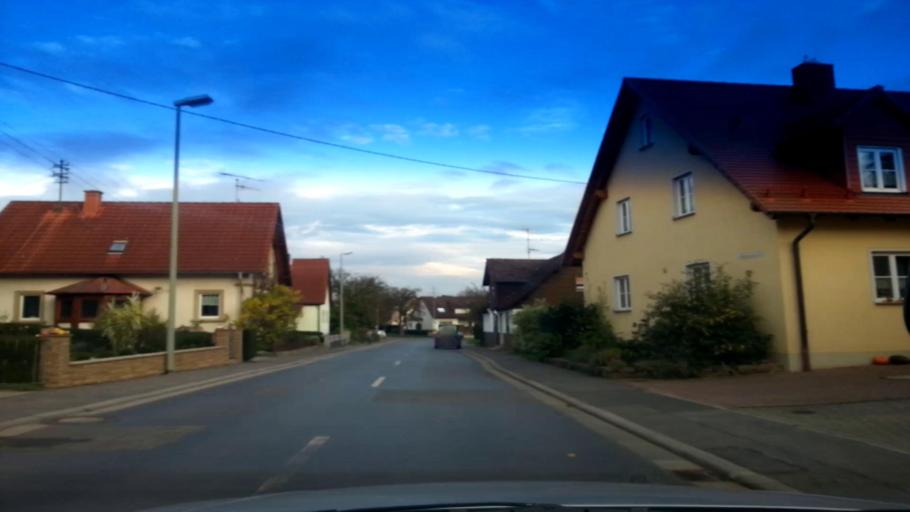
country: DE
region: Bavaria
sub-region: Upper Franconia
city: Memmelsdorf
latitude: 49.9594
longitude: 10.9592
